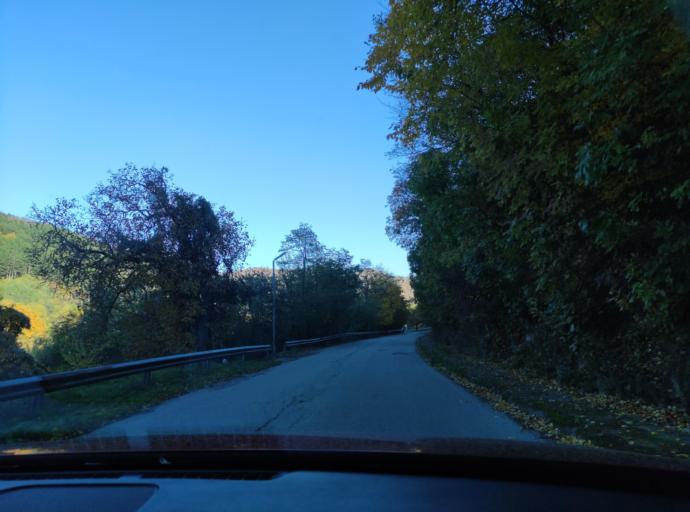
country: BG
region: Montana
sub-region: Obshtina Chiprovtsi
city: Chiprovtsi
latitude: 43.3816
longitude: 22.8960
